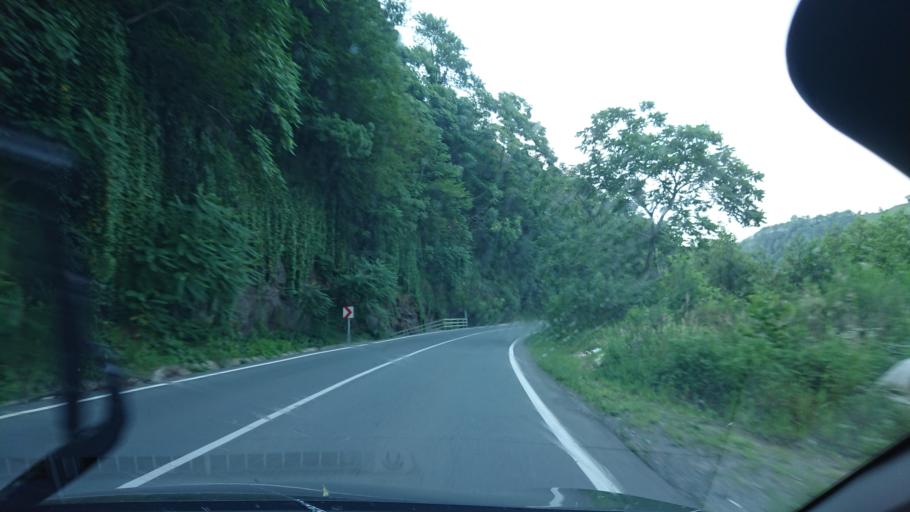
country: TR
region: Rize
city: Cayeli
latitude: 41.0758
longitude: 40.7111
